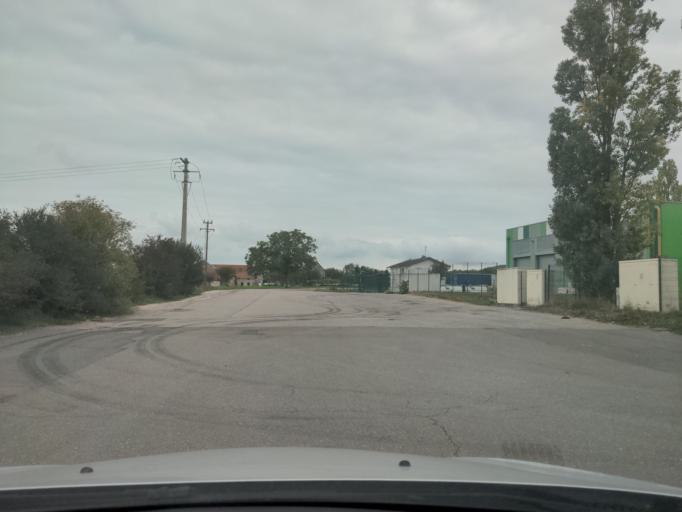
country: FR
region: Bourgogne
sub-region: Departement de la Cote-d'Or
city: Ahuy
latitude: 47.3641
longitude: 5.0376
